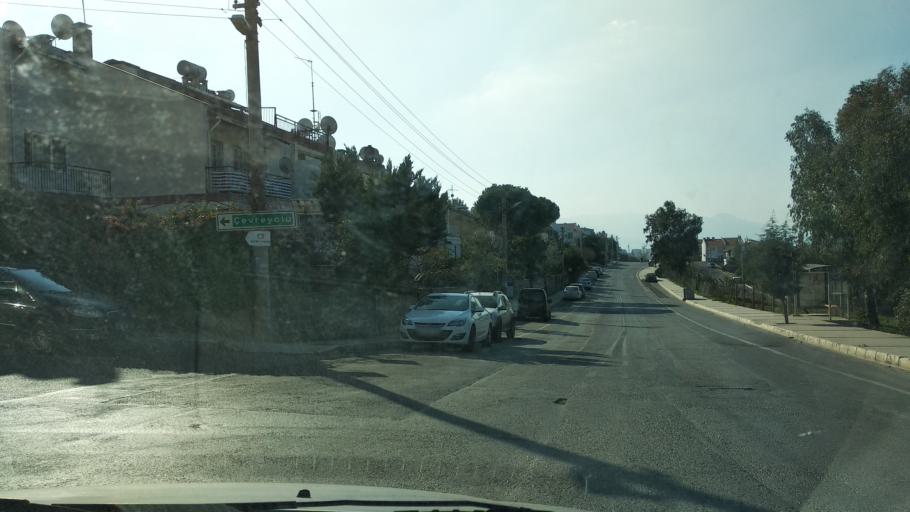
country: TR
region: Izmir
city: Karsiyaka
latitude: 38.4938
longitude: 27.0838
